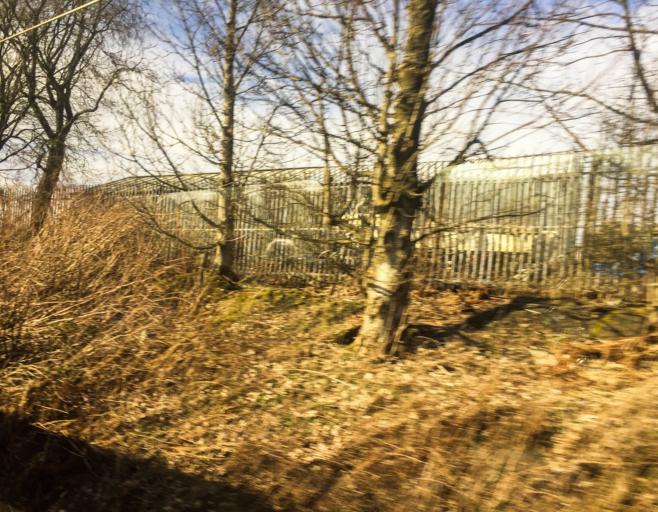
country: GB
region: Scotland
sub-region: North Lanarkshire
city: Chryston
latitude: 55.8911
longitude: -4.1152
